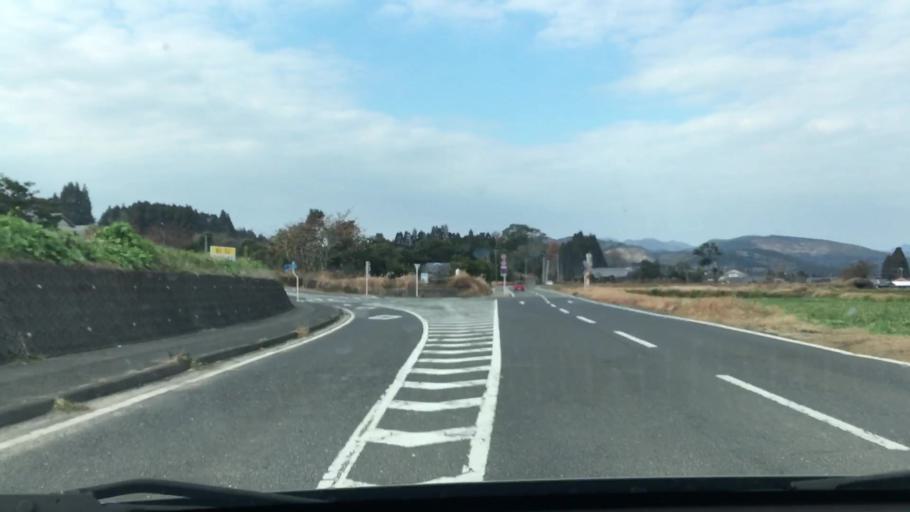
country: JP
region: Miyazaki
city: Kushima
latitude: 31.5196
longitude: 131.2377
